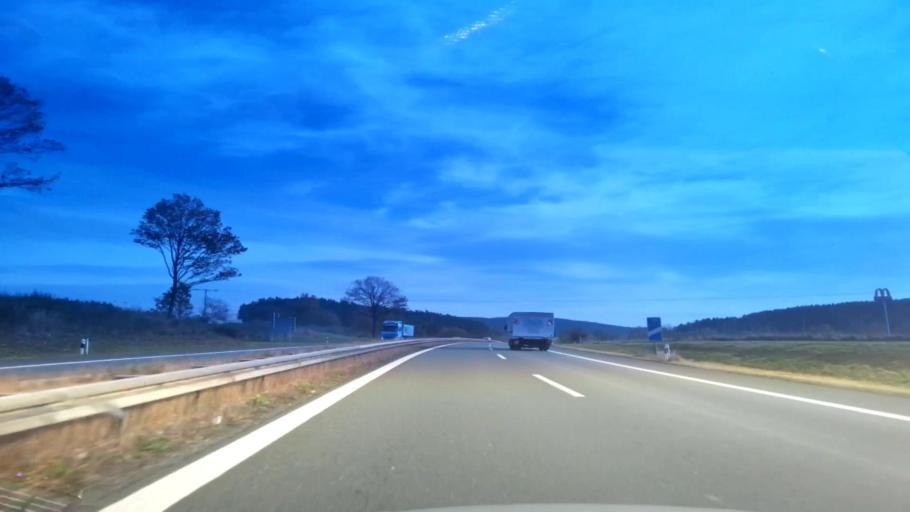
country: DE
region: Bavaria
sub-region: Upper Franconia
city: Neudrossenfeld
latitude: 50.0382
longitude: 11.4871
